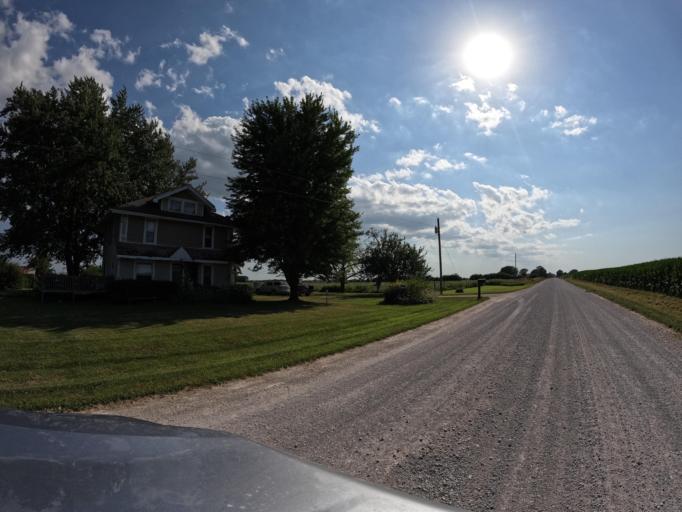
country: US
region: Iowa
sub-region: Appanoose County
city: Centerville
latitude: 40.7179
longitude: -93.0079
